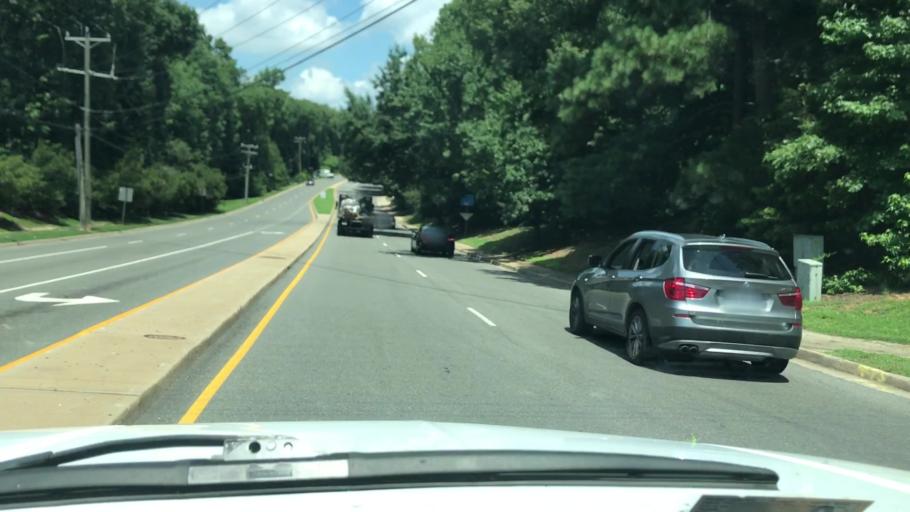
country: US
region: Virginia
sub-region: Henrico County
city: Tuckahoe
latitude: 37.6076
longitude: -77.5904
